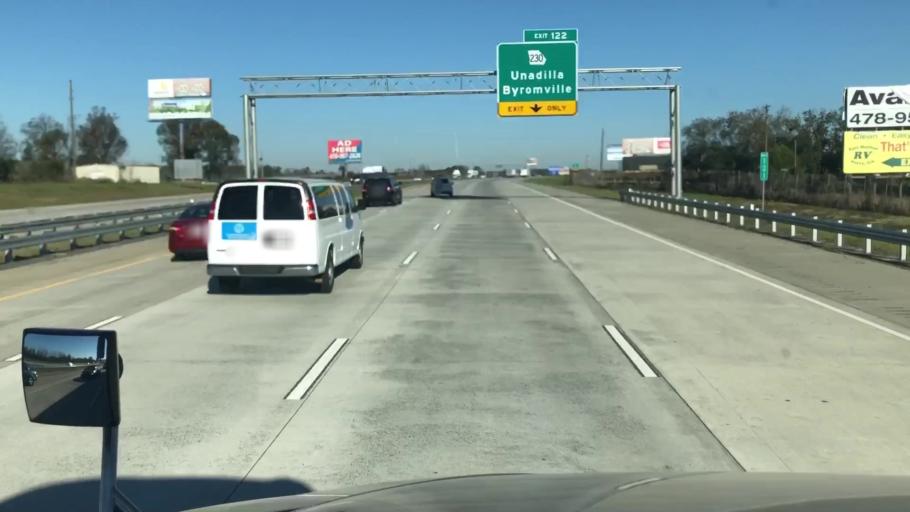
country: US
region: Georgia
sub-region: Dooly County
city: Unadilla
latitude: 32.2525
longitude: -83.7462
